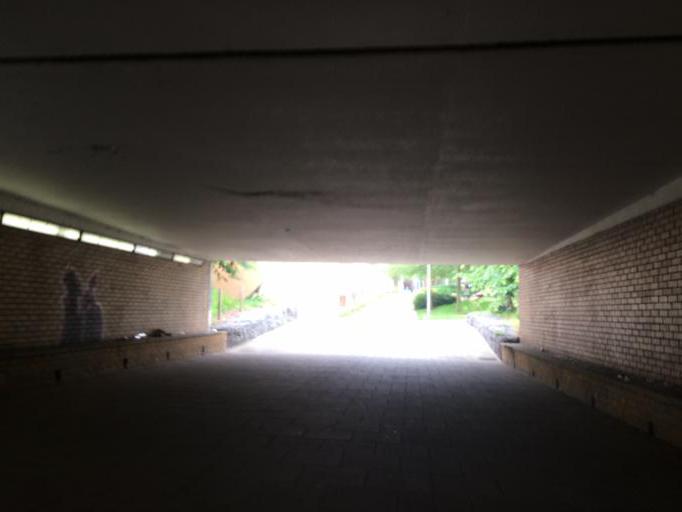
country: GB
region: England
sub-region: Milton Keynes
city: Milton Keynes
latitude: 52.0350
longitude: -0.7595
